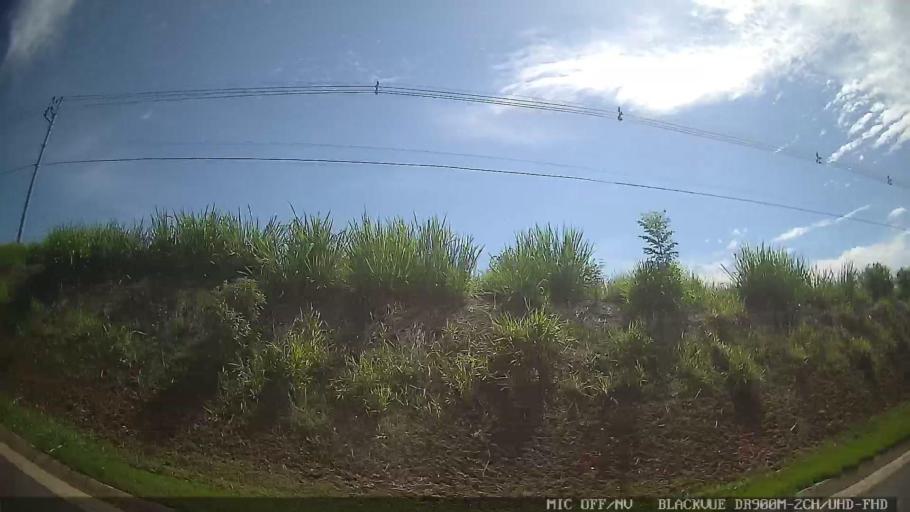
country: BR
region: Sao Paulo
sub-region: Porto Feliz
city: Porto Feliz
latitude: -23.2014
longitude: -47.6047
